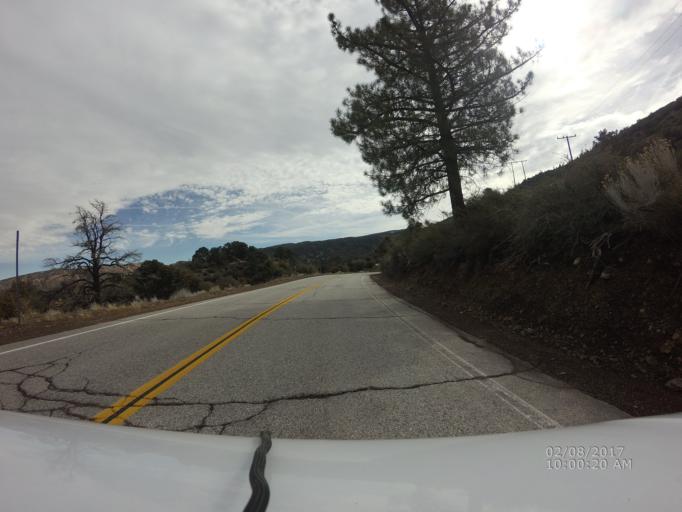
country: US
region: California
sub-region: San Bernardino County
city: Pinon Hills
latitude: 34.4049
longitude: -117.7591
